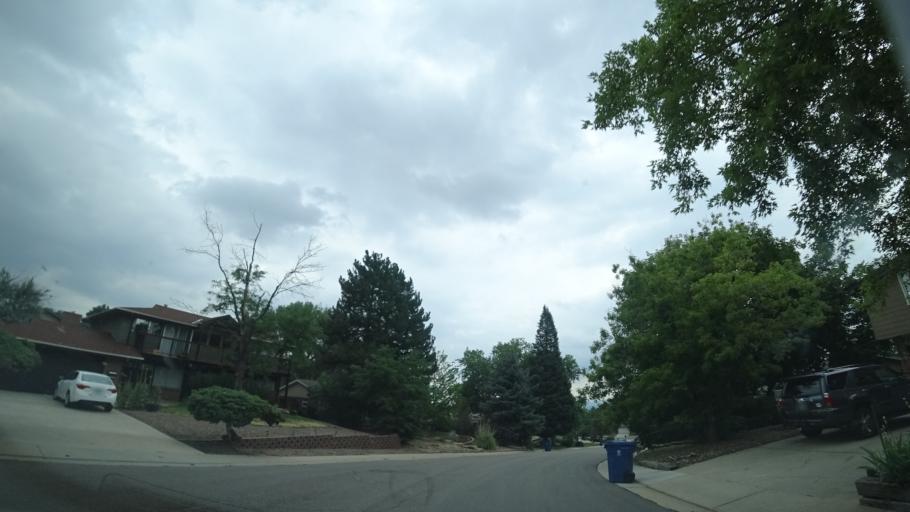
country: US
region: Colorado
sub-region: Jefferson County
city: West Pleasant View
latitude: 39.7016
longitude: -105.1516
